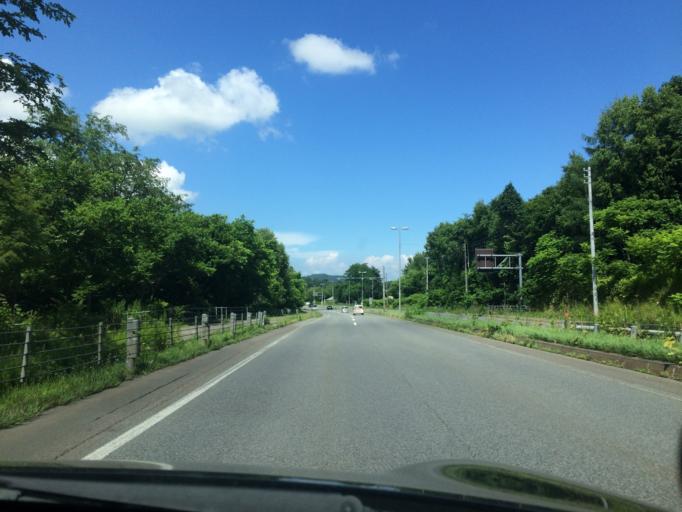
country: JP
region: Hokkaido
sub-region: Asahikawa-shi
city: Asahikawa
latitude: 43.7610
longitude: 142.2786
